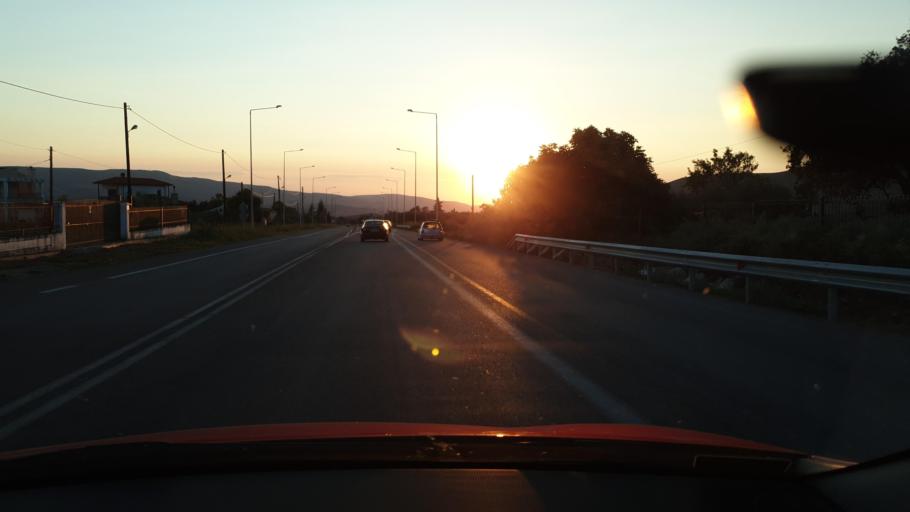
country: GR
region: Central Macedonia
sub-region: Nomos Chalkidikis
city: Galatista
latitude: 40.4665
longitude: 23.2388
